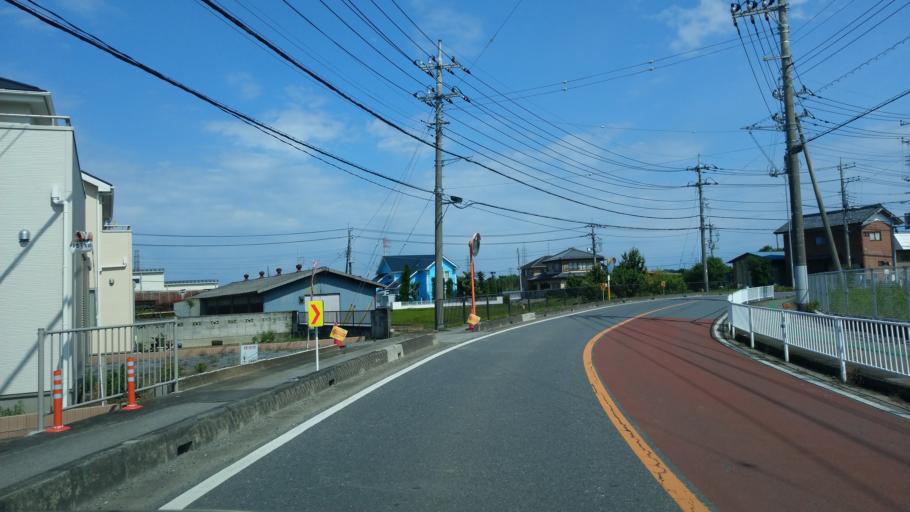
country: JP
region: Saitama
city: Kodamacho-kodamaminami
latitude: 36.2099
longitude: 139.1514
